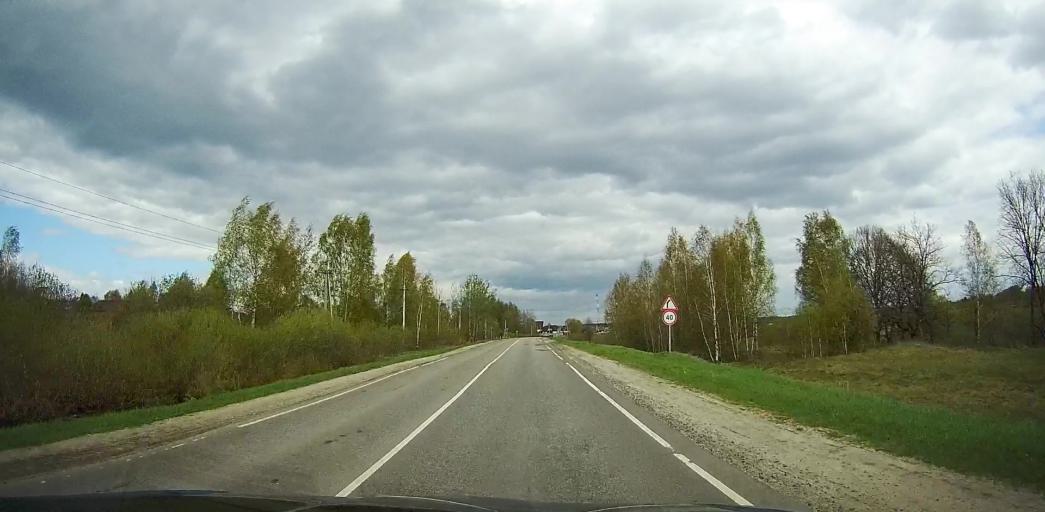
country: RU
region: Moskovskaya
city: Imeni Tsyurupy
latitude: 55.4912
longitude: 38.6201
